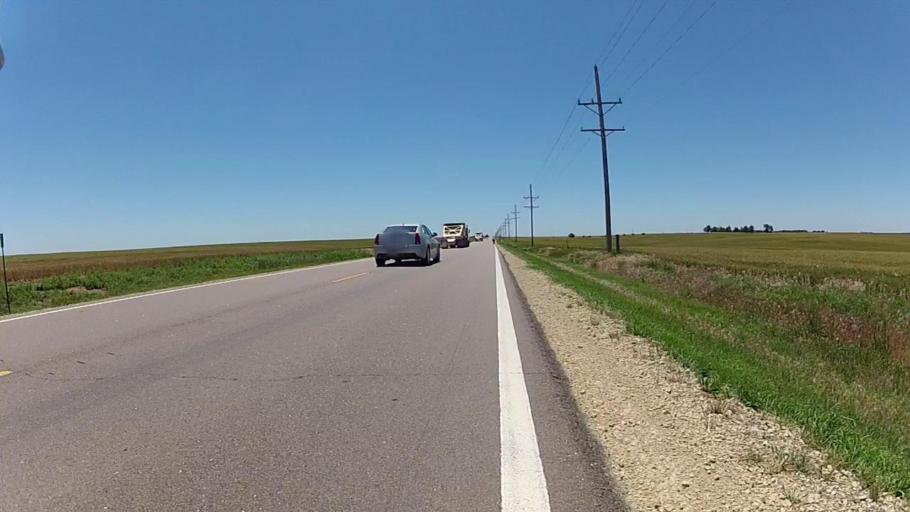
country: US
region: Kansas
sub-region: Kiowa County
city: Greensburg
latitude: 37.5328
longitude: -99.3208
